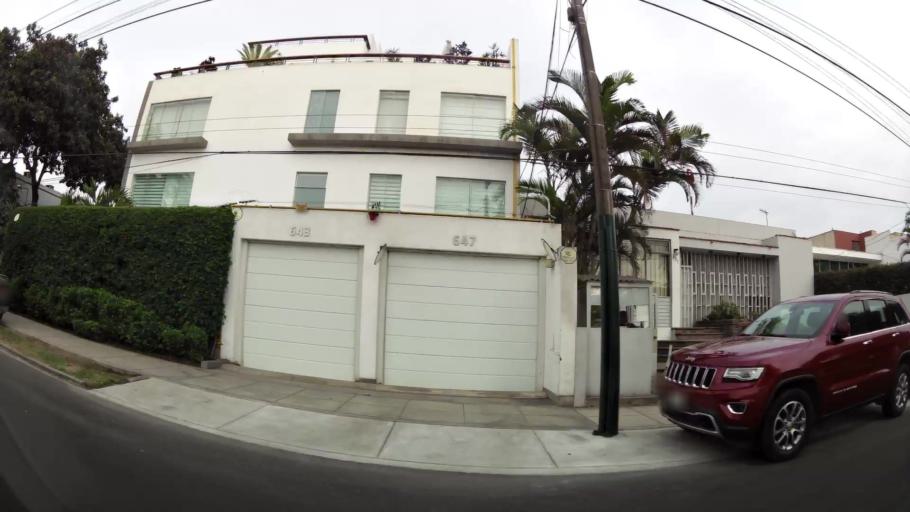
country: PE
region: Lima
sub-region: Lima
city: San Isidro
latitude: -12.1071
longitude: -77.0531
